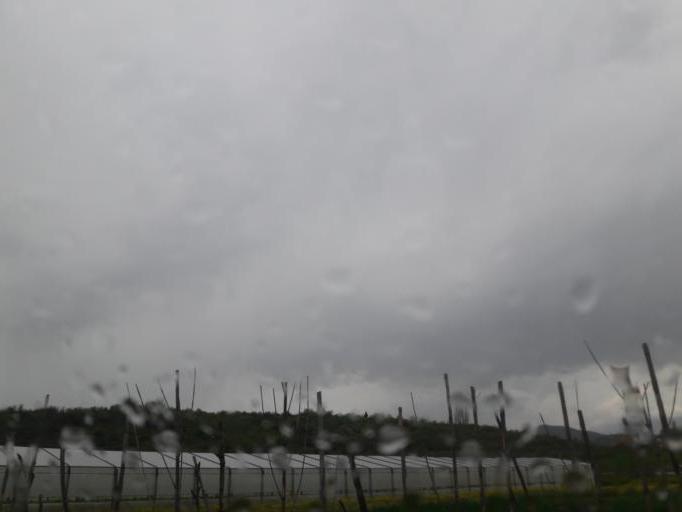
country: AL
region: Shkoder
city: Vukatane
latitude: 42.0133
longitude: 19.5449
